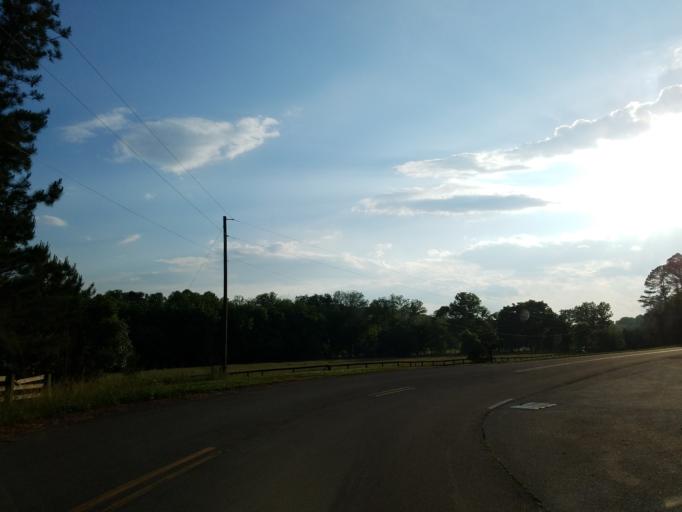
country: US
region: Georgia
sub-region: Cherokee County
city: Ball Ground
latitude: 34.2982
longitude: -84.3760
